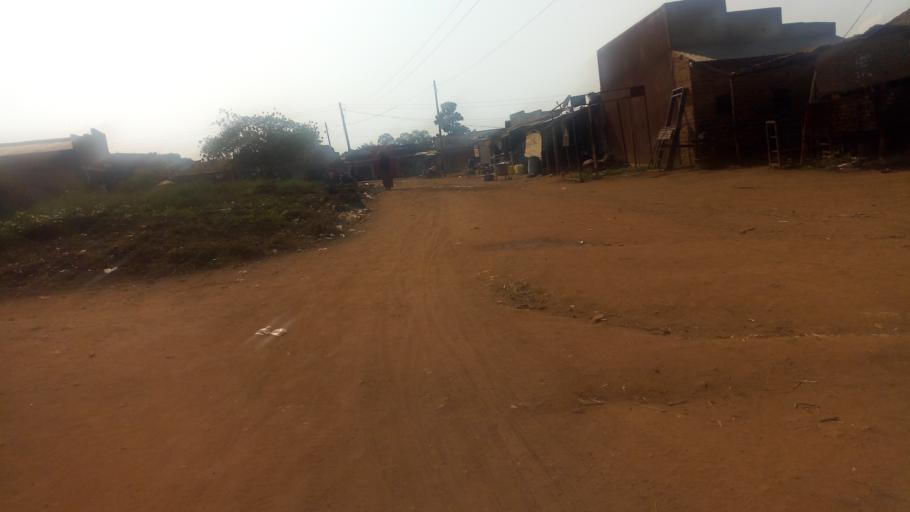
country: UG
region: Western Region
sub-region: Kiryandongo District
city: Kiryandongo
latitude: 1.8094
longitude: 32.0092
